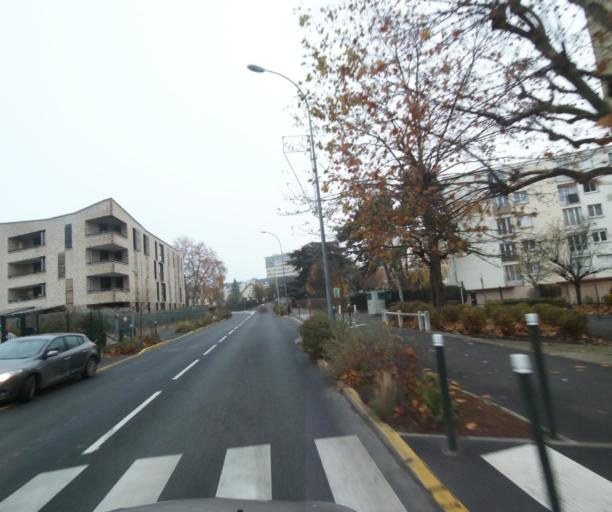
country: FR
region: Ile-de-France
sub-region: Departement de Seine-Saint-Denis
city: Gagny
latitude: 48.8705
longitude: 2.5359
